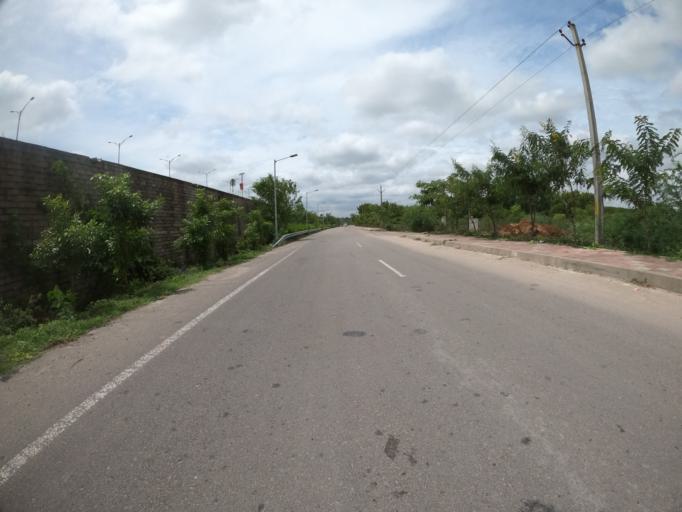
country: IN
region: Telangana
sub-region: Rangareddi
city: Balapur
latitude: 17.2853
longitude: 78.3823
